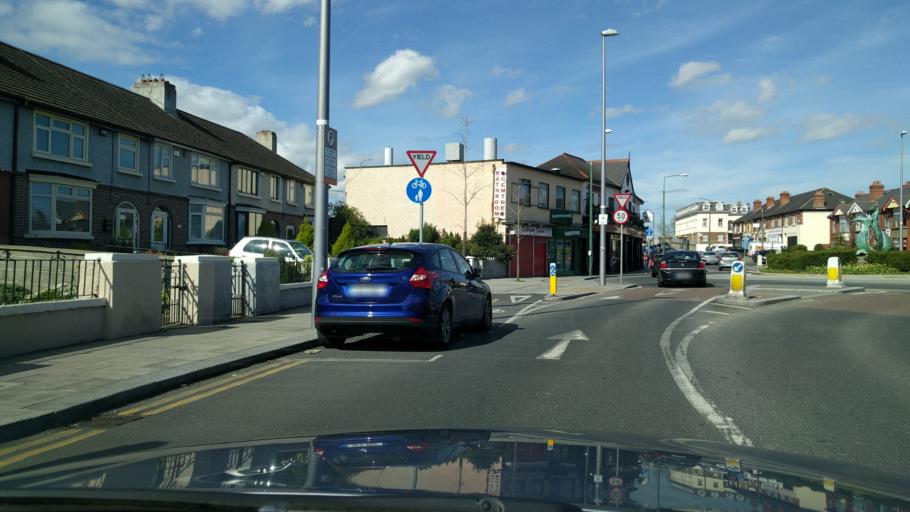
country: IE
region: Leinster
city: Rialto
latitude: 53.3359
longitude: -6.2991
